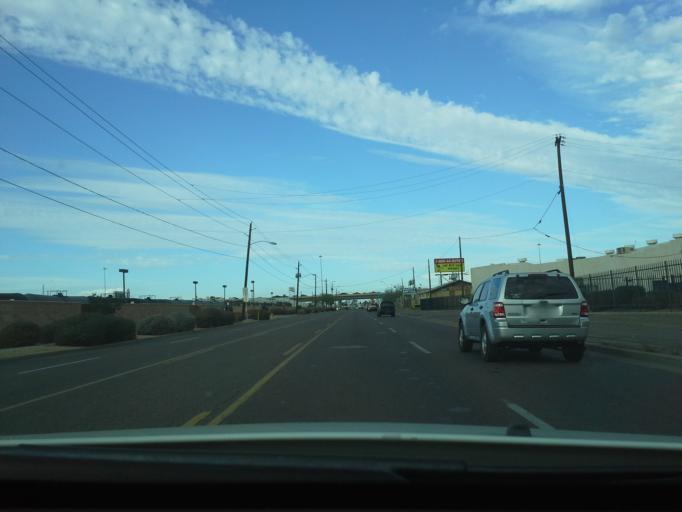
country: US
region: Arizona
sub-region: Maricopa County
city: Phoenix
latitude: 33.4574
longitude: -112.1000
